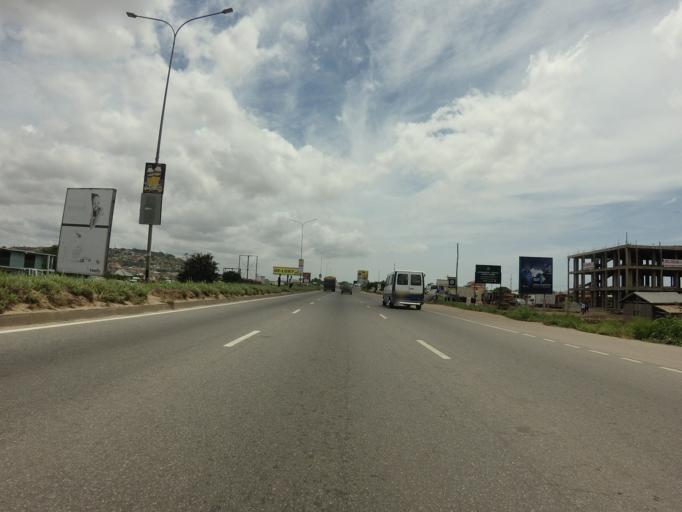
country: GH
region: Greater Accra
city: Gbawe
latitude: 5.5534
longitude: -0.3161
